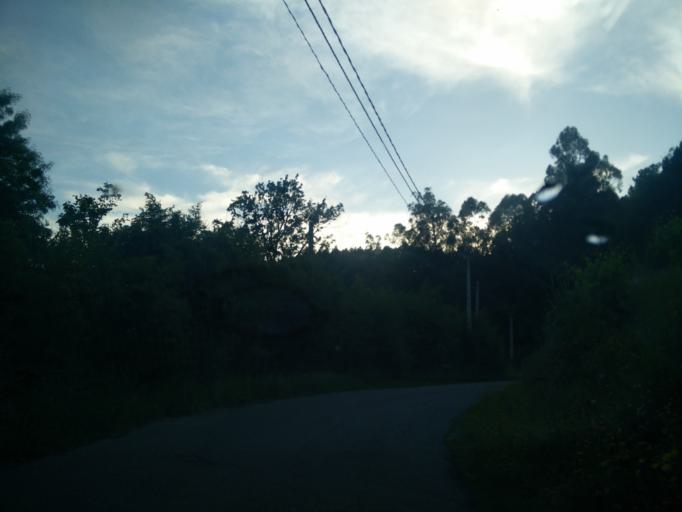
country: ES
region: Galicia
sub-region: Provincia de Pontevedra
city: Mondariz
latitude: 42.2526
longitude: -8.4257
